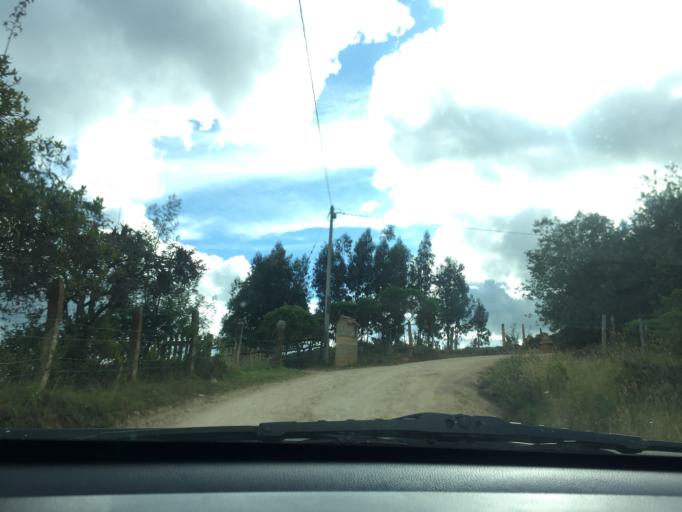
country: CO
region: Cundinamarca
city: Tocancipa
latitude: 4.9287
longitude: -73.8943
